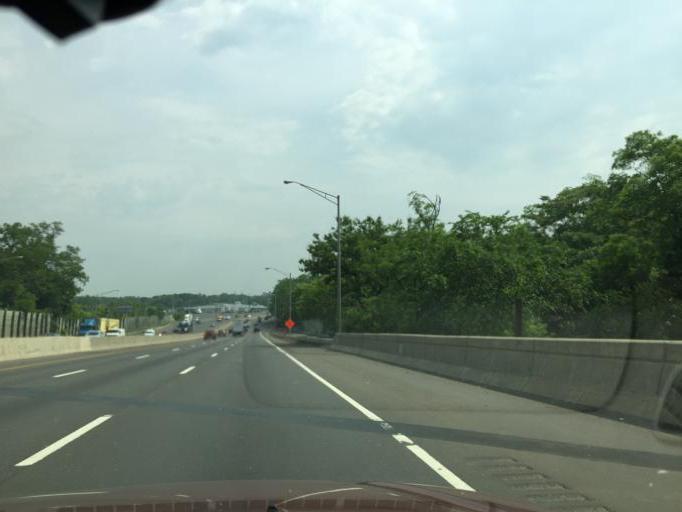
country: US
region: Connecticut
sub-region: Fairfield County
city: Stamford
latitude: 41.0630
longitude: -73.5082
